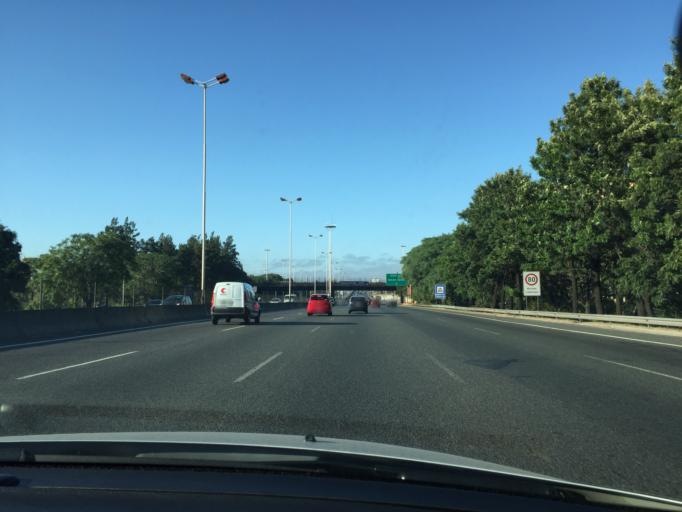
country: AR
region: Buenos Aires F.D.
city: Villa Lugano
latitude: -34.7038
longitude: -58.4995
